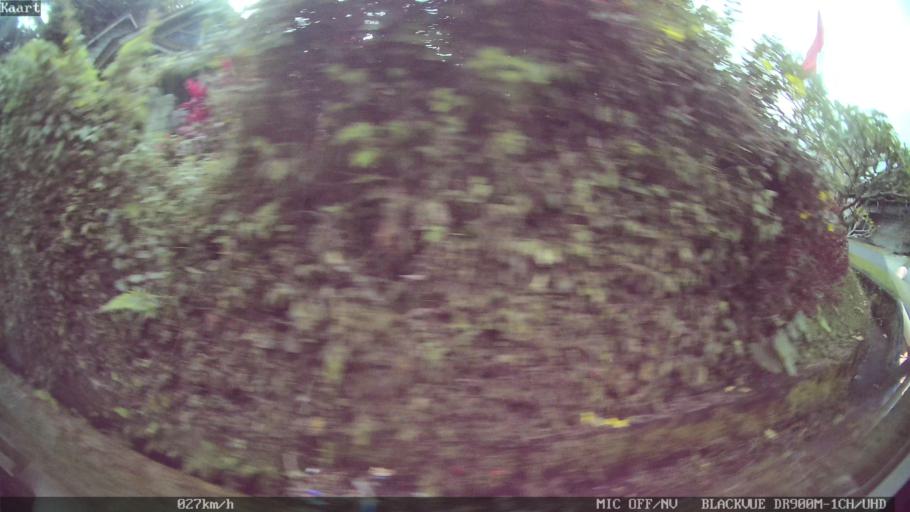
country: ID
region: Bali
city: Banjar Pesalakan
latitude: -8.4963
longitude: 115.3046
